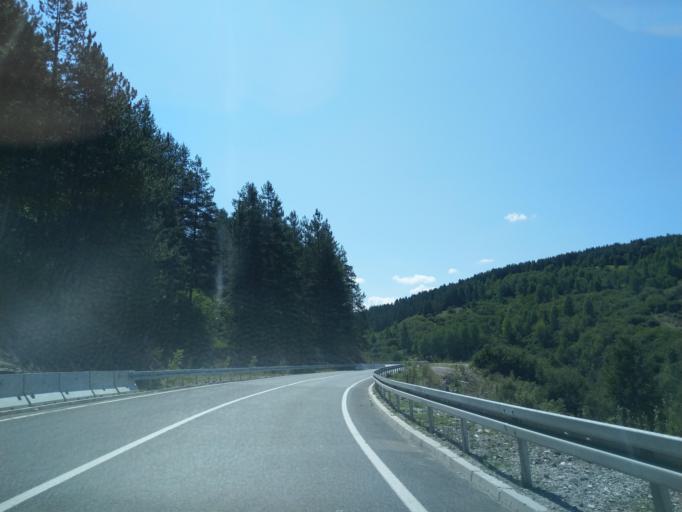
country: RS
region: Central Serbia
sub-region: Zlatiborski Okrug
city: Sjenica
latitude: 43.2852
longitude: 19.9466
